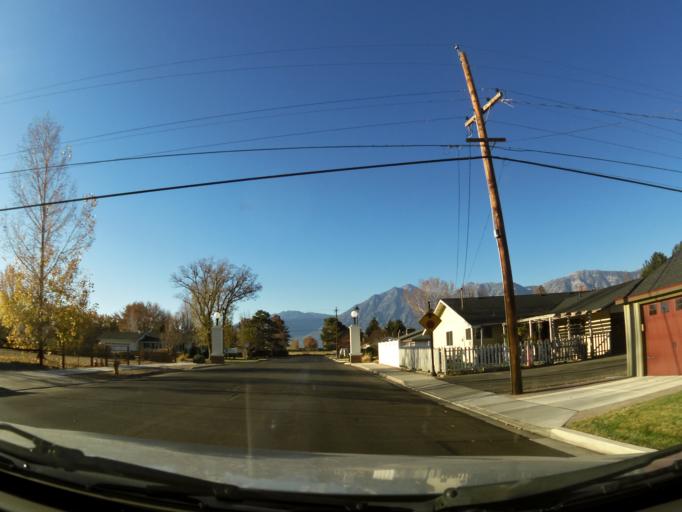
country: US
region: Nevada
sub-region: Douglas County
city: Minden
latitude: 38.9531
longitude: -119.7663
